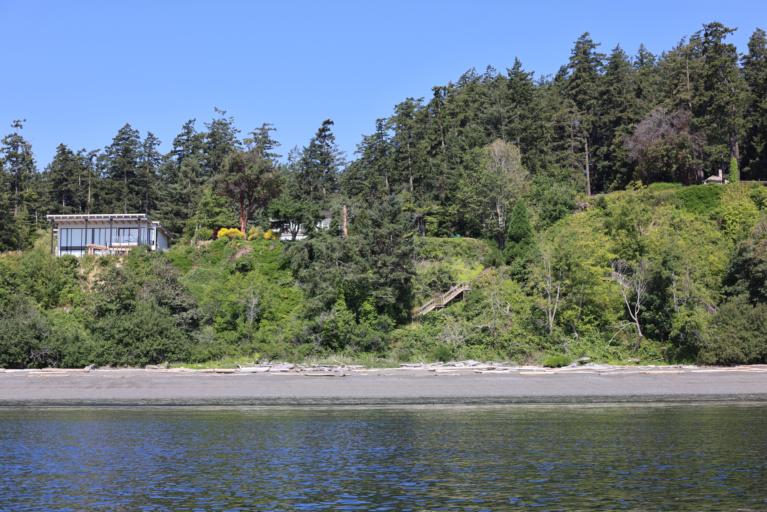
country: CA
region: British Columbia
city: Colwood
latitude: 48.3986
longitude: -123.4850
